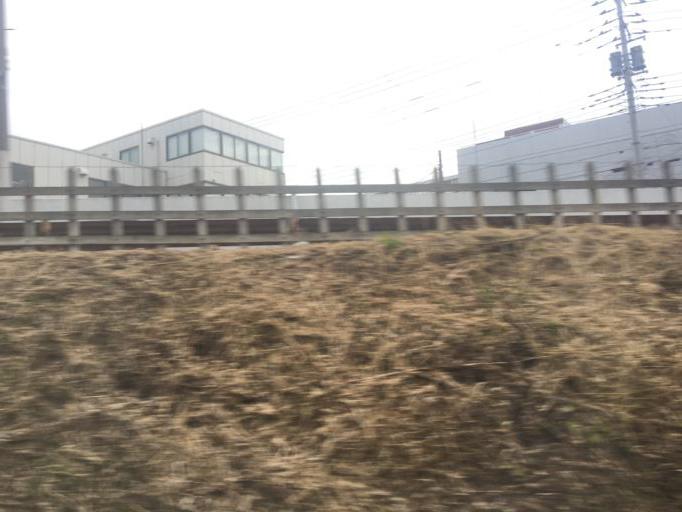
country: JP
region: Tokyo
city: Hachioji
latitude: 35.6658
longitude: 139.3613
